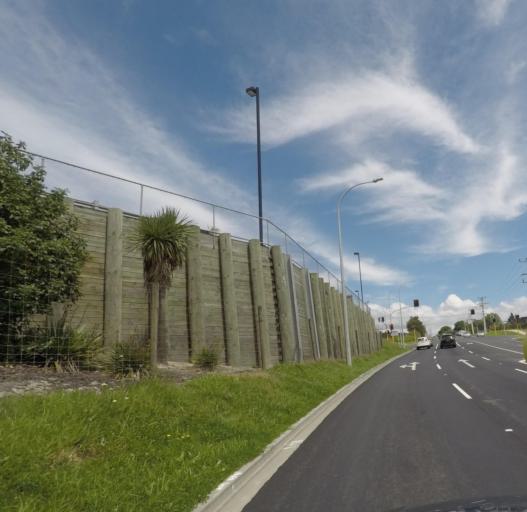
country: NZ
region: Auckland
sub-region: Auckland
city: Rothesay Bay
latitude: -36.6240
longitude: 174.6726
